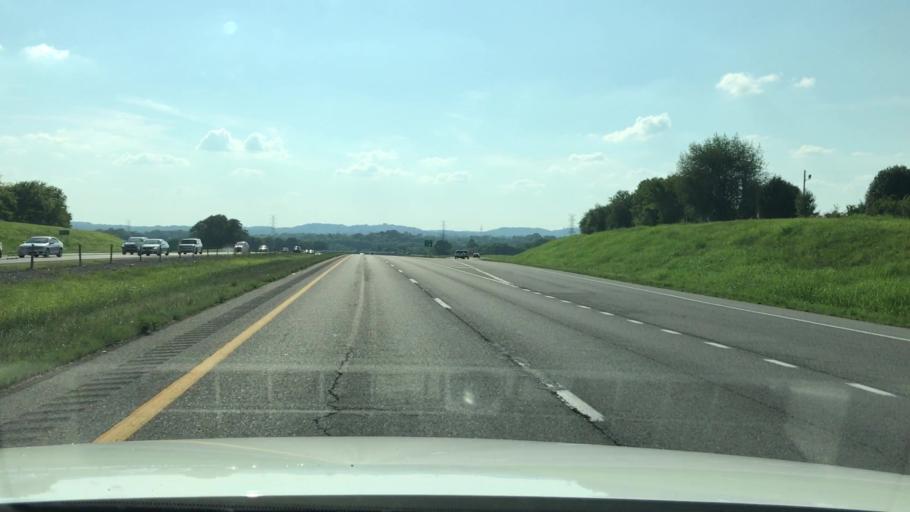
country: US
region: Tennessee
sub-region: Sumner County
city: Hendersonville
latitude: 36.3321
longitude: -86.5865
